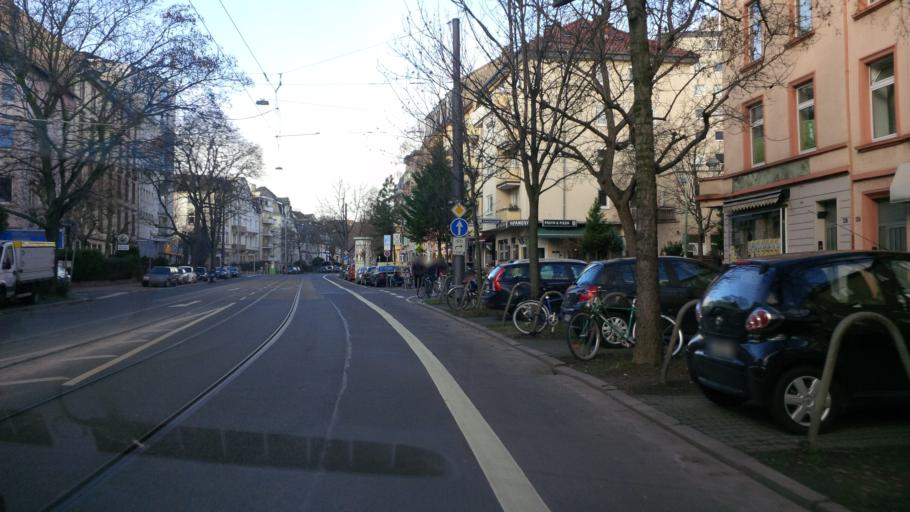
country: DE
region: Hesse
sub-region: Regierungsbezirk Darmstadt
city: Frankfurt am Main
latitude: 50.1271
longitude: 8.6855
